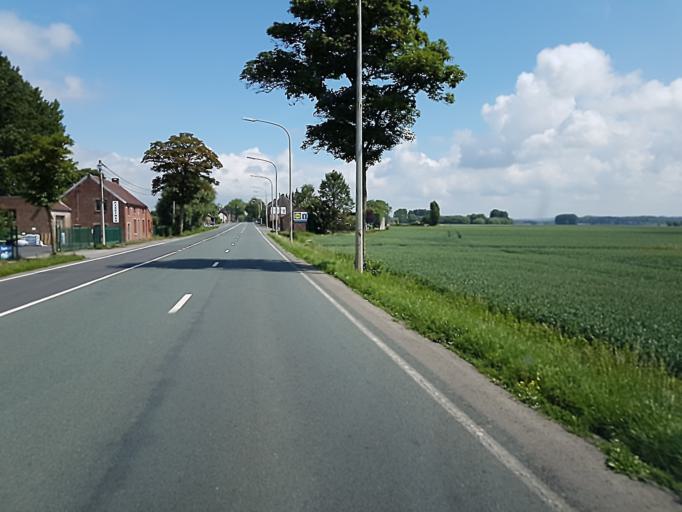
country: BE
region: Wallonia
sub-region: Province du Hainaut
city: Soignies
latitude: 50.5496
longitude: 4.0504
